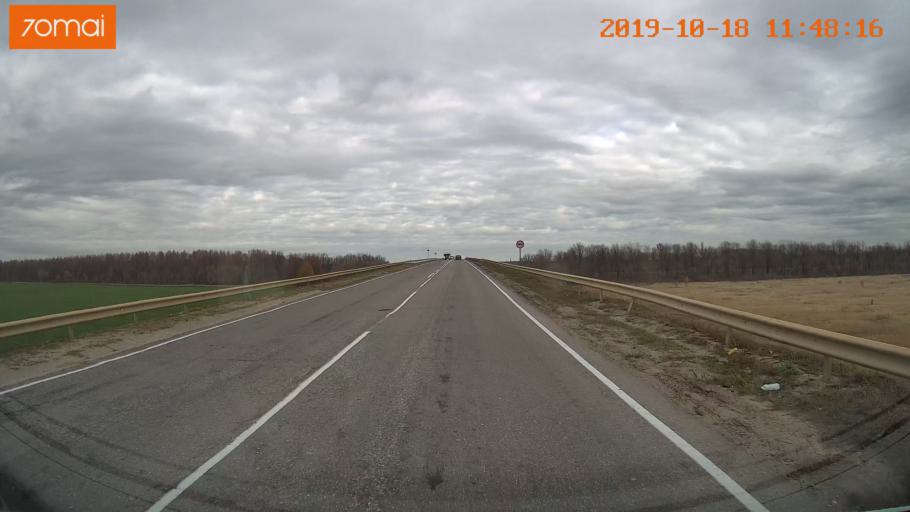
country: RU
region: Rjazan
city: Mikhaylov
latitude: 54.2378
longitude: 38.9819
